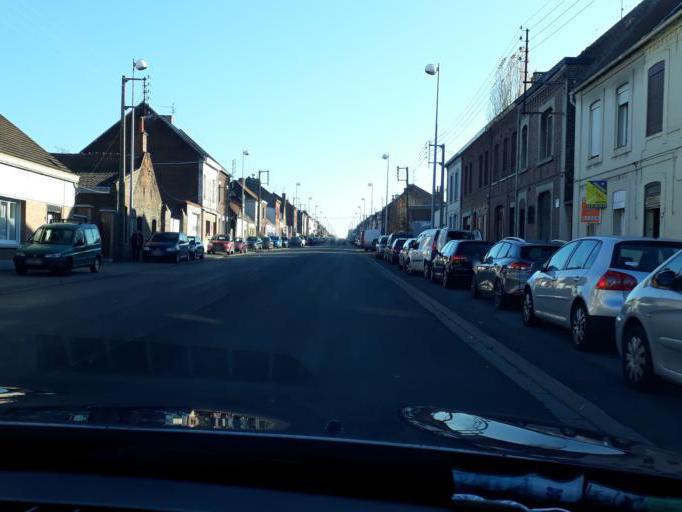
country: FR
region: Nord-Pas-de-Calais
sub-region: Departement du Nord
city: Aniche
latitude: 50.3284
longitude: 3.2454
